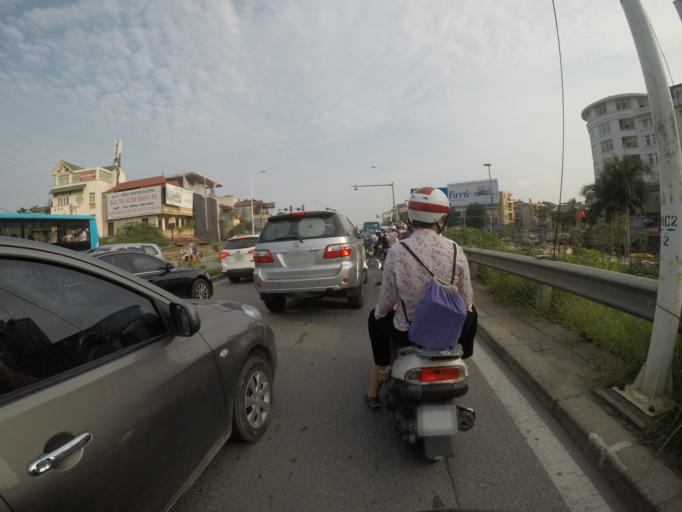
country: VN
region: Ha Noi
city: Tay Ho
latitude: 21.0817
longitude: 105.8177
